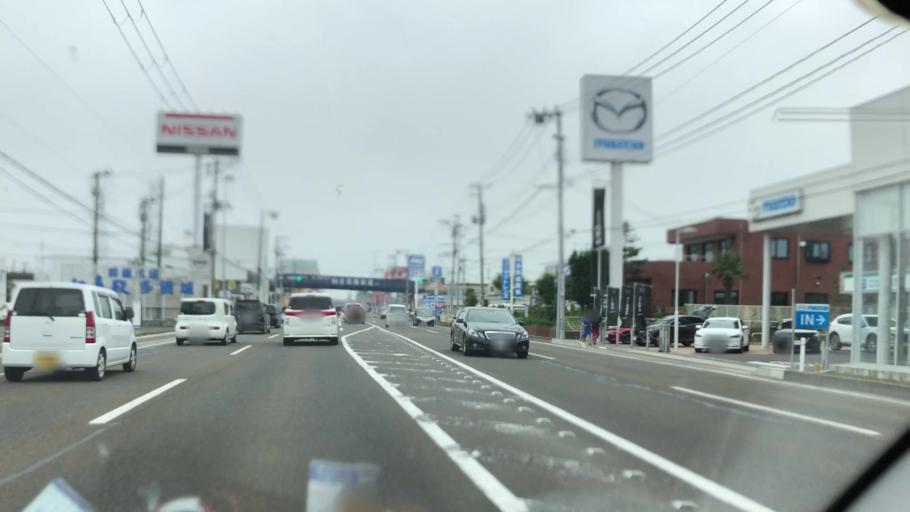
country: JP
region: Miyagi
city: Shiogama
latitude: 38.2850
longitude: 141.0019
